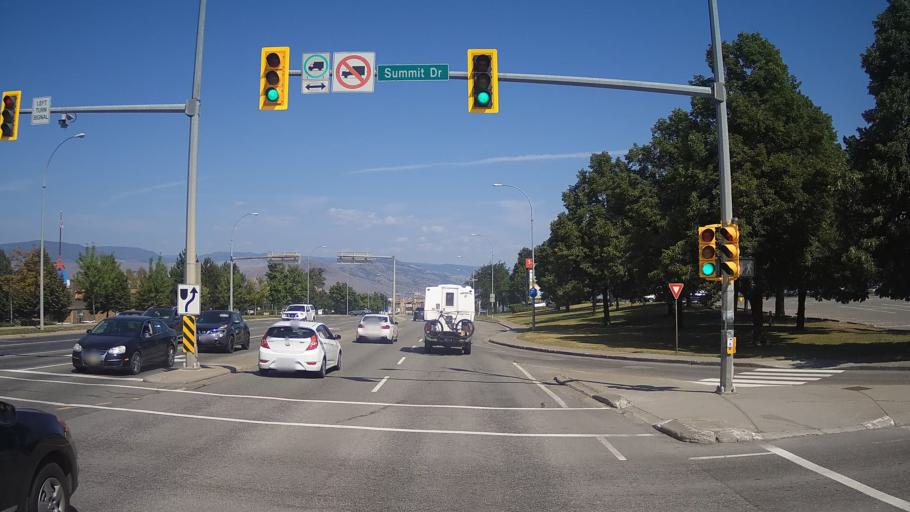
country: CA
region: British Columbia
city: Kamloops
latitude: 50.6668
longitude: -120.3541
